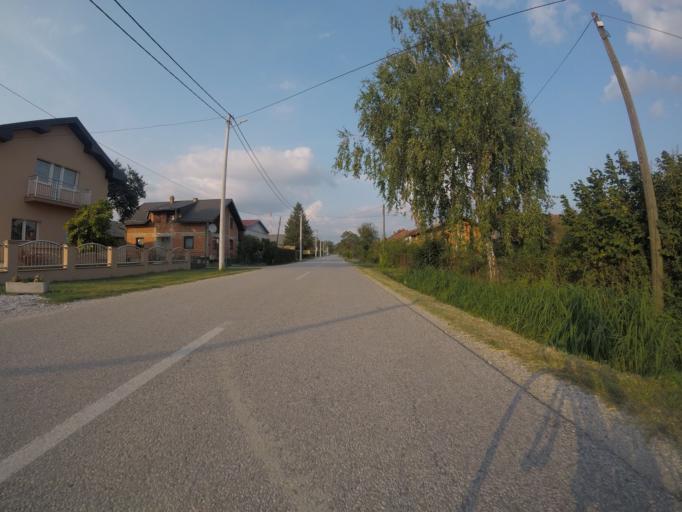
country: HR
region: Zagrebacka
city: Kuce
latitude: 45.7214
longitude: 16.2044
